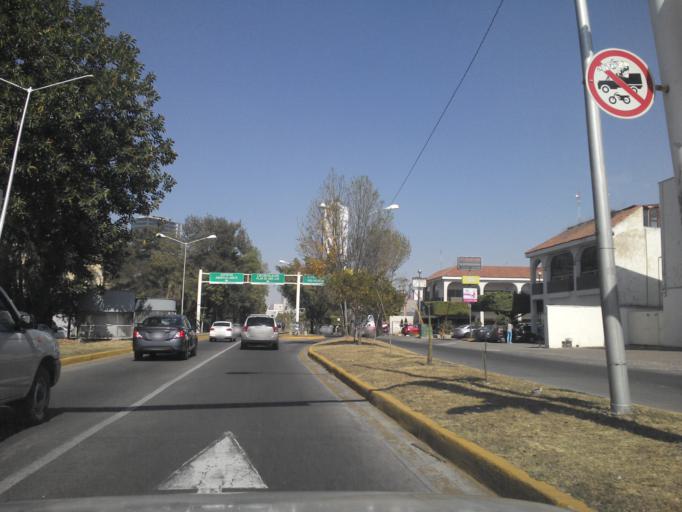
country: MX
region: Jalisco
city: Guadalajara
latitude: 20.6921
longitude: -103.3757
